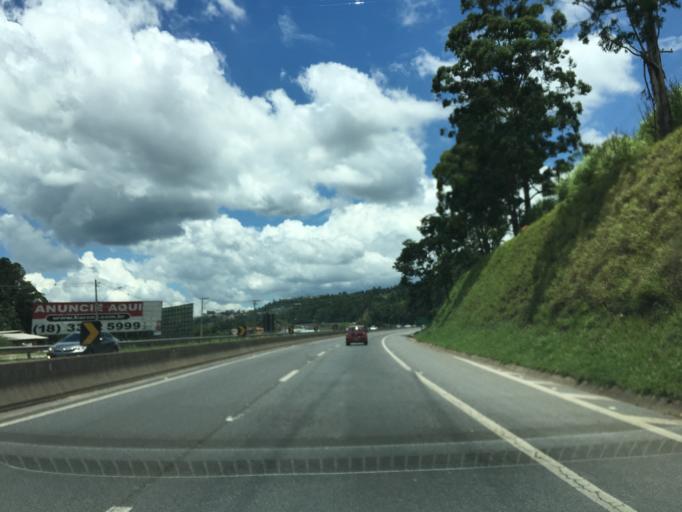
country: BR
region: Sao Paulo
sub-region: Mairipora
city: Mairipora
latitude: -23.2387
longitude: -46.5989
